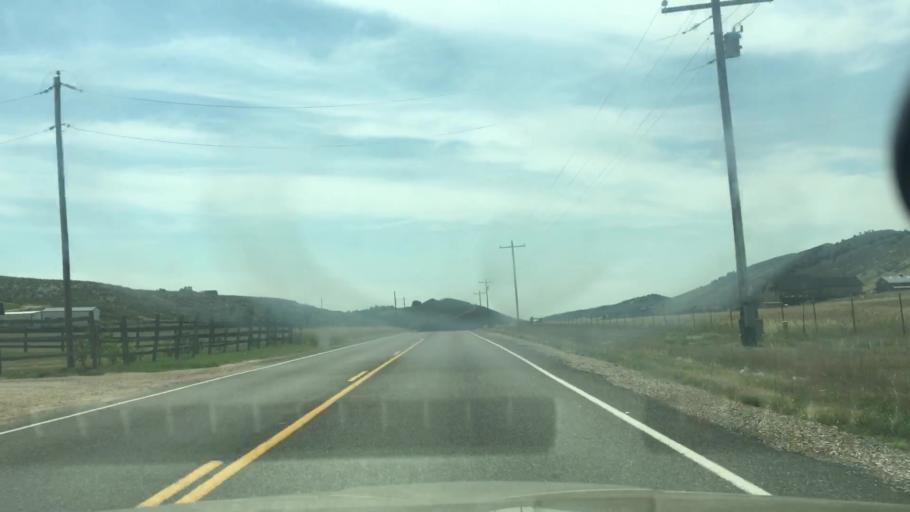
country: US
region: Colorado
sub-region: Larimer County
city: Campion
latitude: 40.3492
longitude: -105.1840
